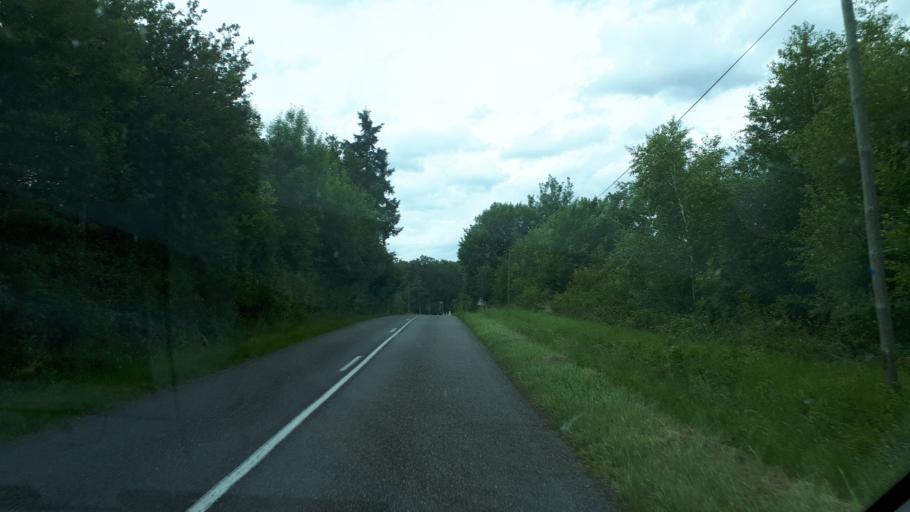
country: FR
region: Centre
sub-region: Departement du Loir-et-Cher
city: Villefranche-sur-Cher
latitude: 47.2172
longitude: 1.7698
